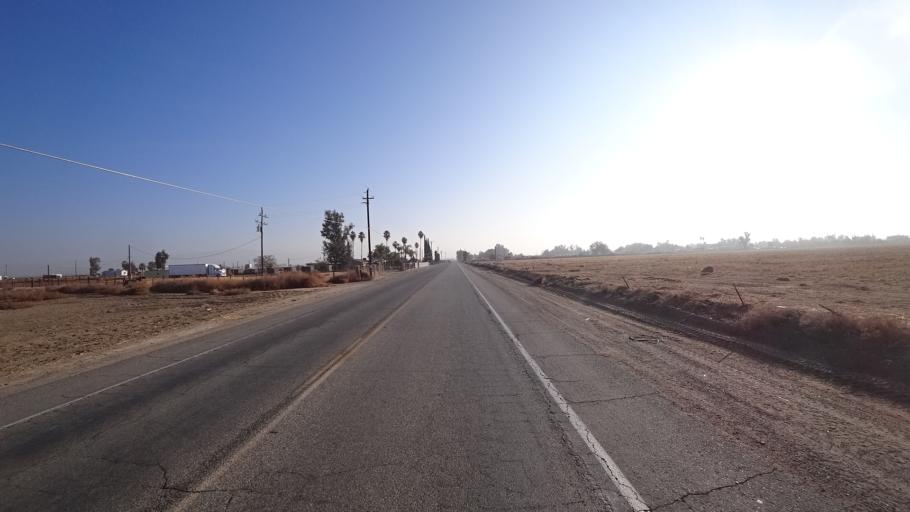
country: US
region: California
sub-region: Kern County
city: Greenfield
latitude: 35.2524
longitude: -118.9709
